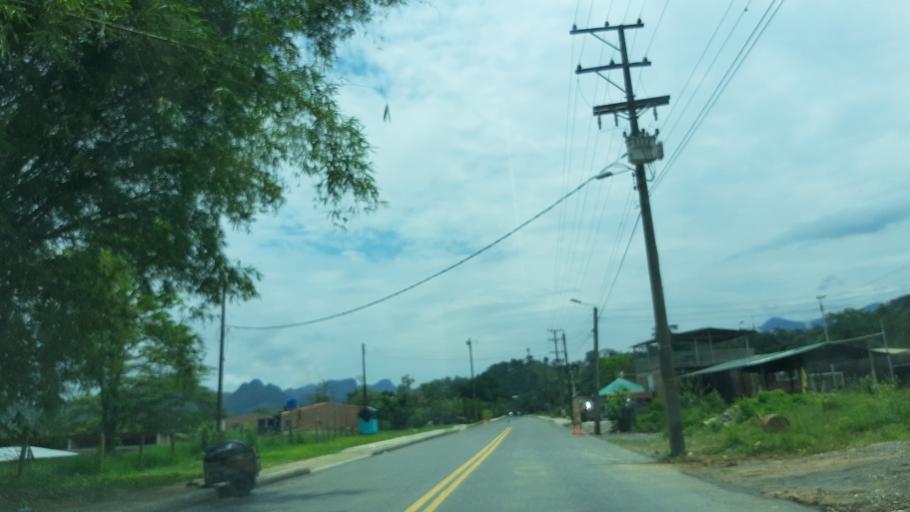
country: CO
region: Boyaca
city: San Luis de Gaceno
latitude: 4.8266
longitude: -73.1628
